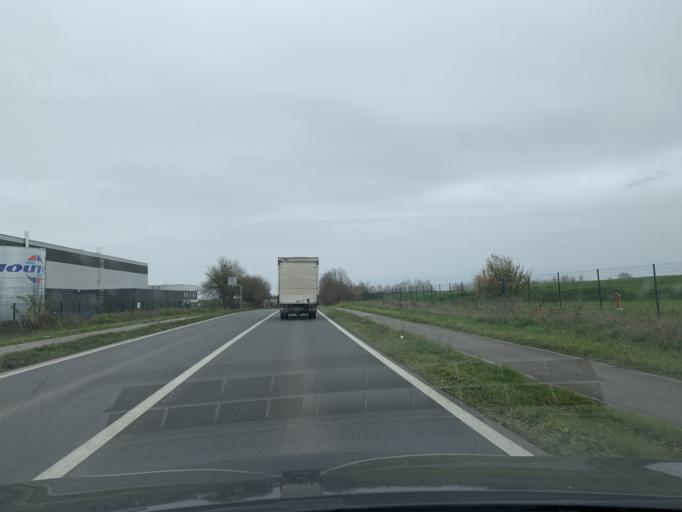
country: FR
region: Nord-Pas-de-Calais
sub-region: Departement du Nord
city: Neuville-Saint-Remy
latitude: 50.1984
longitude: 3.2046
